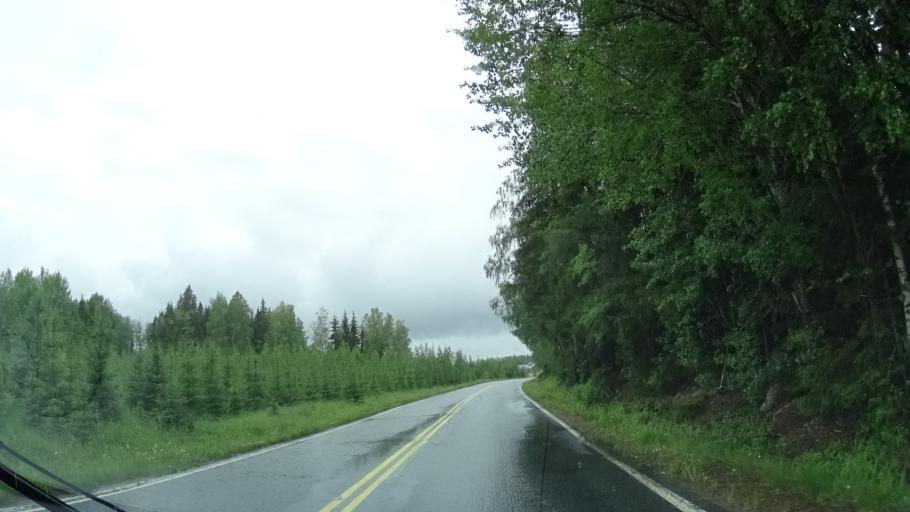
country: FI
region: Haeme
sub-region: Forssa
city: Humppila
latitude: 60.9927
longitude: 23.2560
